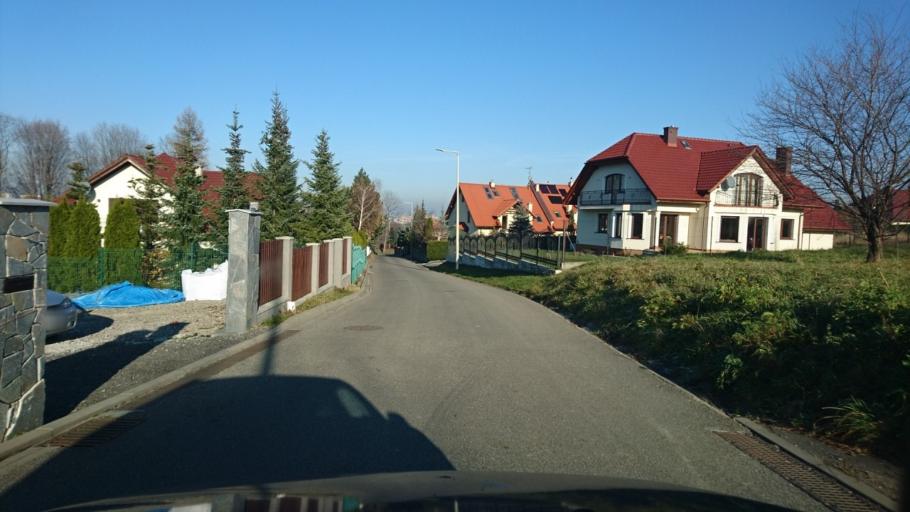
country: PL
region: Silesian Voivodeship
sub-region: Bielsko-Biala
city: Bielsko-Biala
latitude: 49.7922
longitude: 19.0232
